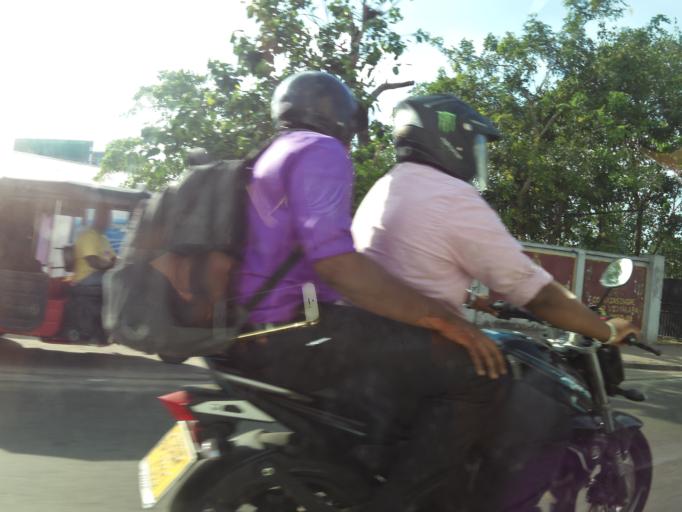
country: LK
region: Western
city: Kolonnawa
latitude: 6.9414
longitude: 79.8783
